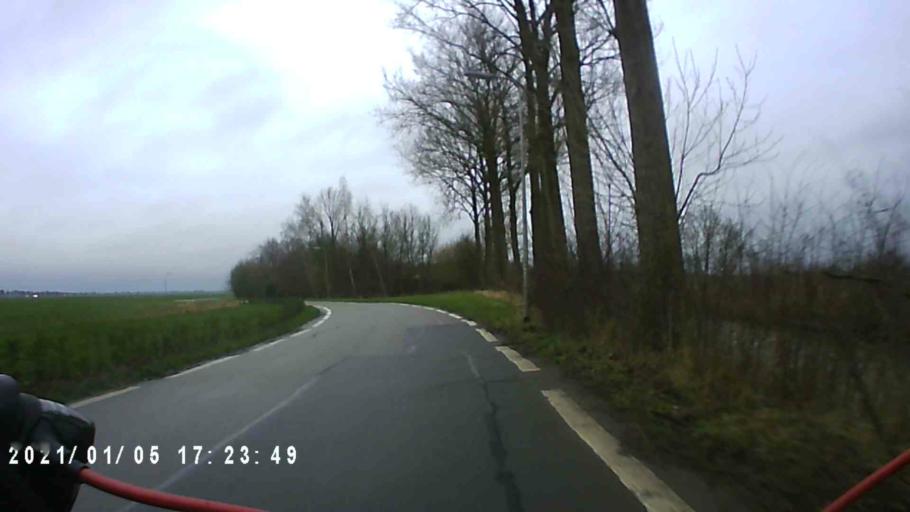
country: NL
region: Groningen
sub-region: Gemeente Delfzijl
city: Delfzijl
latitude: 53.2344
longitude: 6.9643
